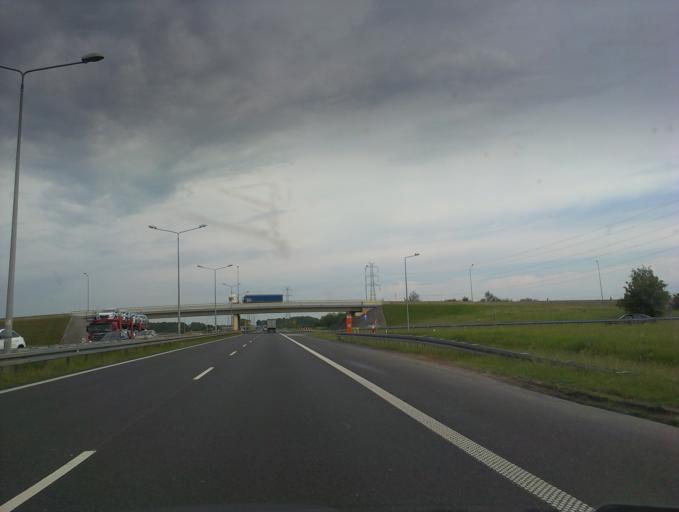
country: PL
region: Opole Voivodeship
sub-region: Powiat brzeski
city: Grodkow
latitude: 50.7820
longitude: 17.3486
